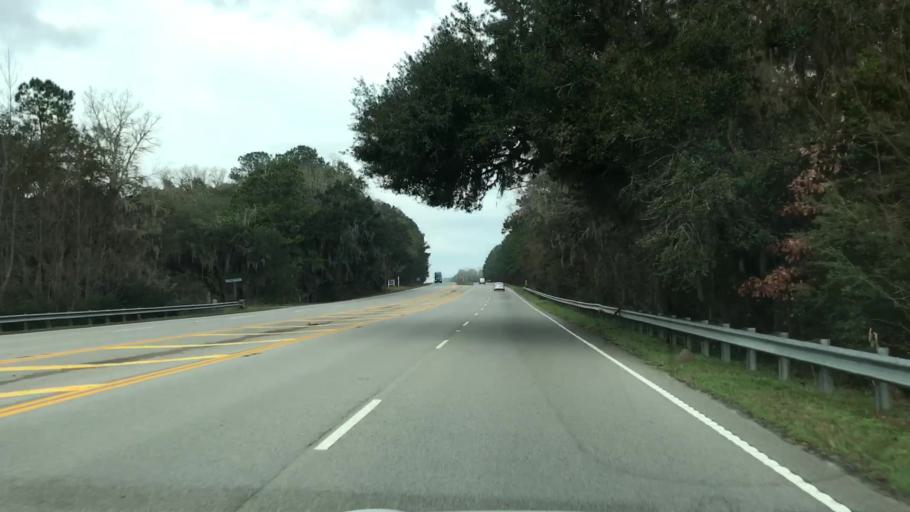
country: US
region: South Carolina
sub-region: Hampton County
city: Yemassee
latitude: 32.6259
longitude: -80.8277
